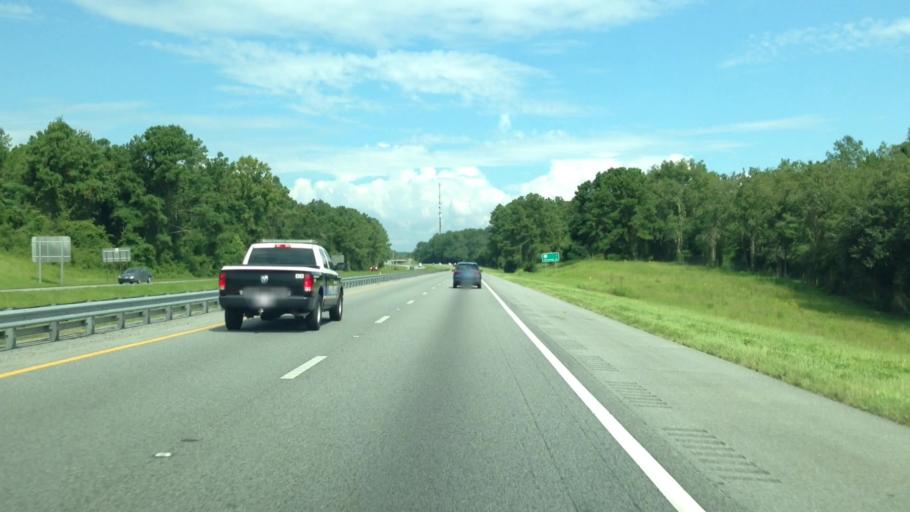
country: US
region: Florida
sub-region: Suwannee County
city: Live Oak
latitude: 30.3399
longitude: -82.9750
